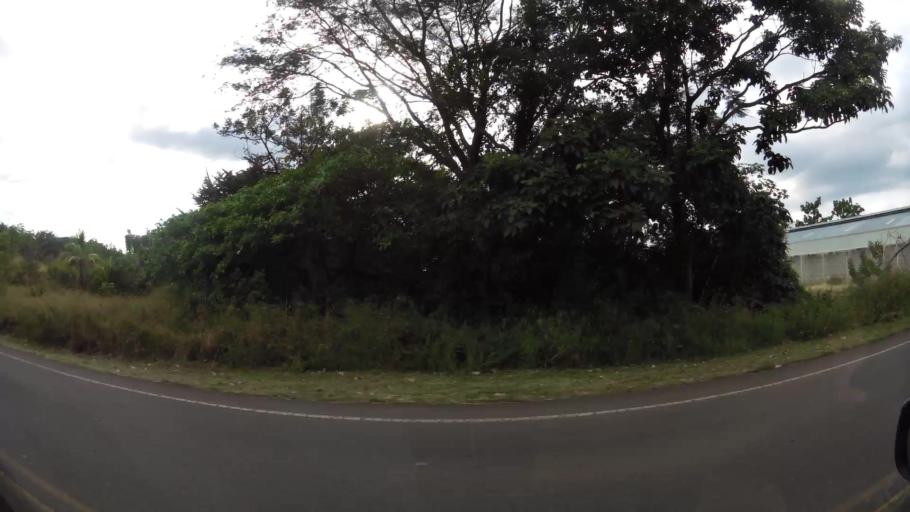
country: CR
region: Alajuela
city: Orotina
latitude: 9.8748
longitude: -84.5737
